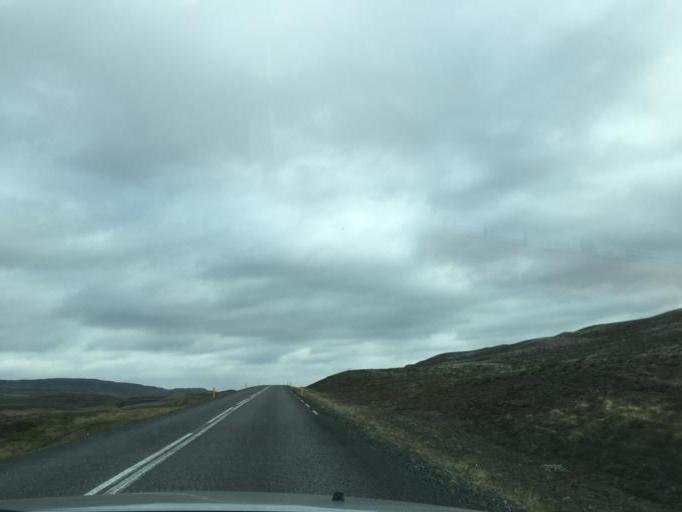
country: IS
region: South
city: Vestmannaeyjar
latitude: 64.2620
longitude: -20.1961
